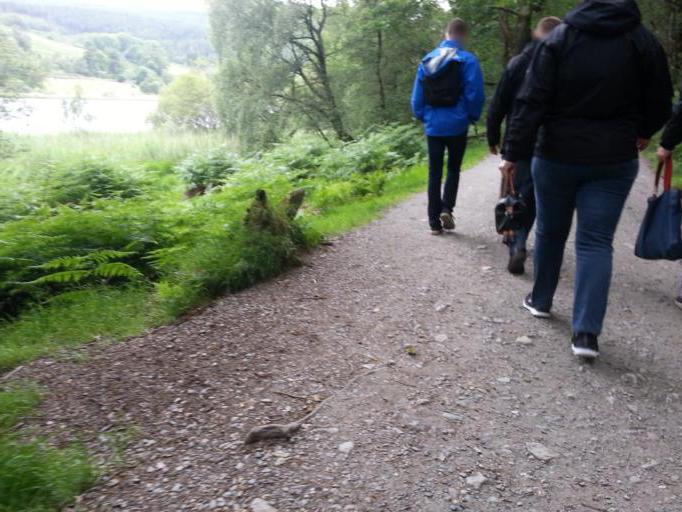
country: IE
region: Leinster
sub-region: Wicklow
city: Rathdrum
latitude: 53.0070
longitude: -6.3376
